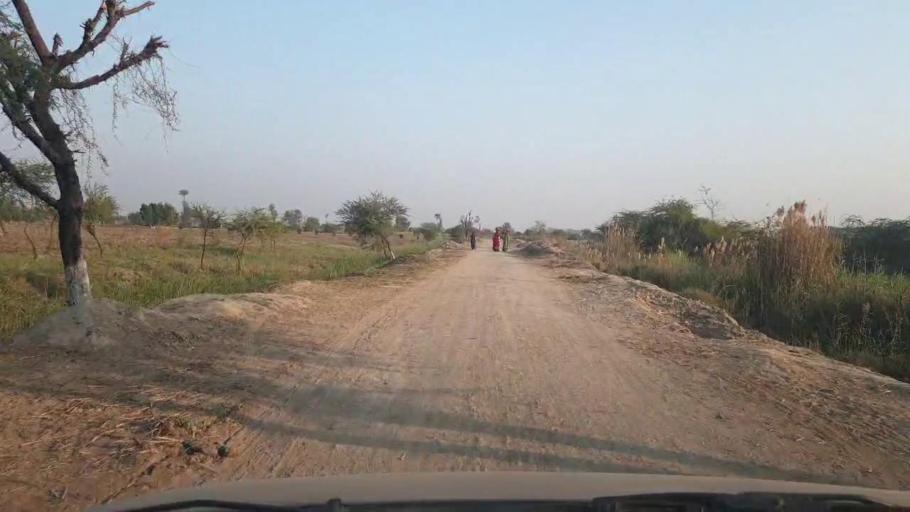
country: PK
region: Sindh
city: Mirwah Gorchani
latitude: 25.3592
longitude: 69.1522
